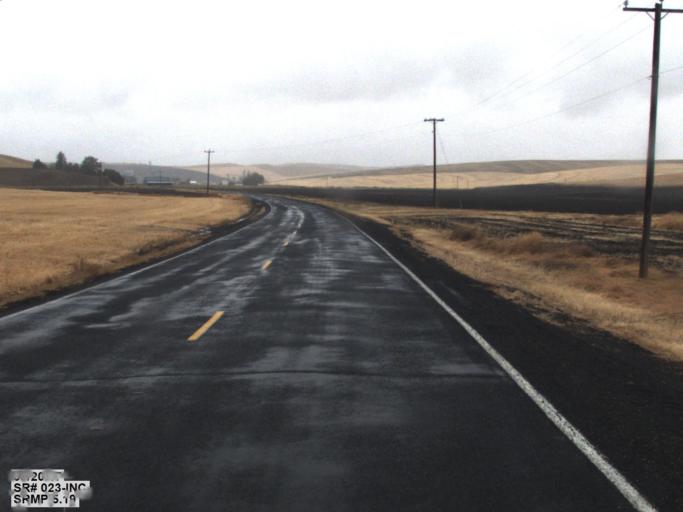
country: US
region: Washington
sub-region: Whitman County
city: Colfax
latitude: 47.0083
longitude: -117.4586
